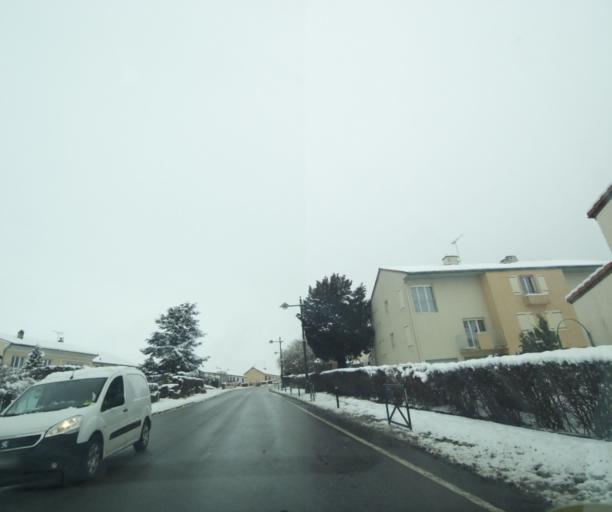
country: FR
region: Champagne-Ardenne
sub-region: Departement de la Haute-Marne
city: Montier-en-Der
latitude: 48.4814
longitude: 4.7695
